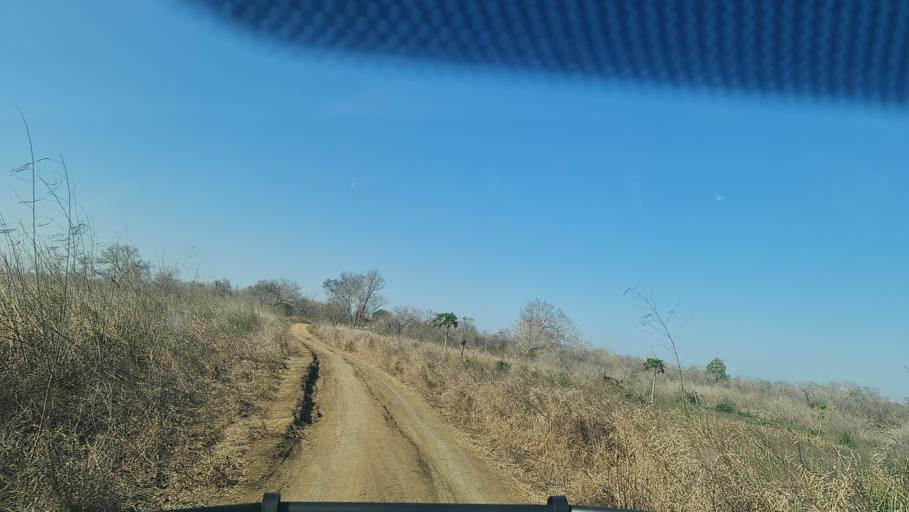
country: MZ
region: Nampula
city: Nacala
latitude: -13.9475
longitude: 40.4789
